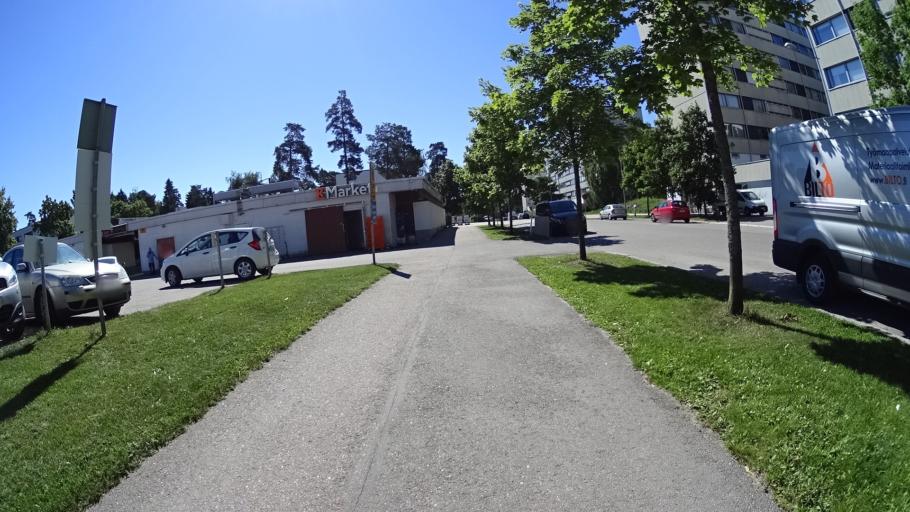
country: FI
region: Uusimaa
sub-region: Helsinki
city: Espoo
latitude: 60.1493
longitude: 24.6910
